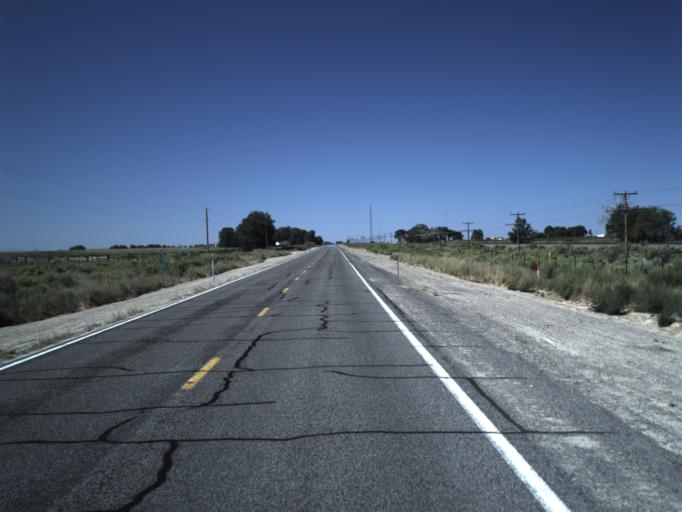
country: US
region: Utah
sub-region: Millard County
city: Delta
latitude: 39.5476
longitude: -112.3585
